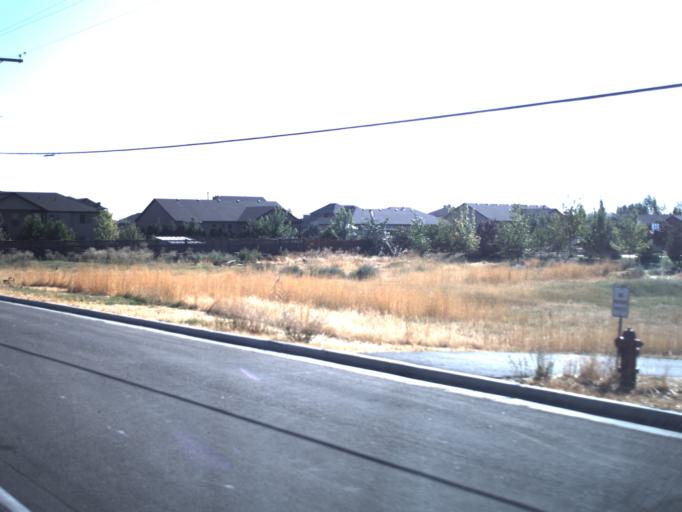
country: US
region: Utah
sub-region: Weber County
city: Hooper
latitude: 41.1705
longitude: -112.1227
